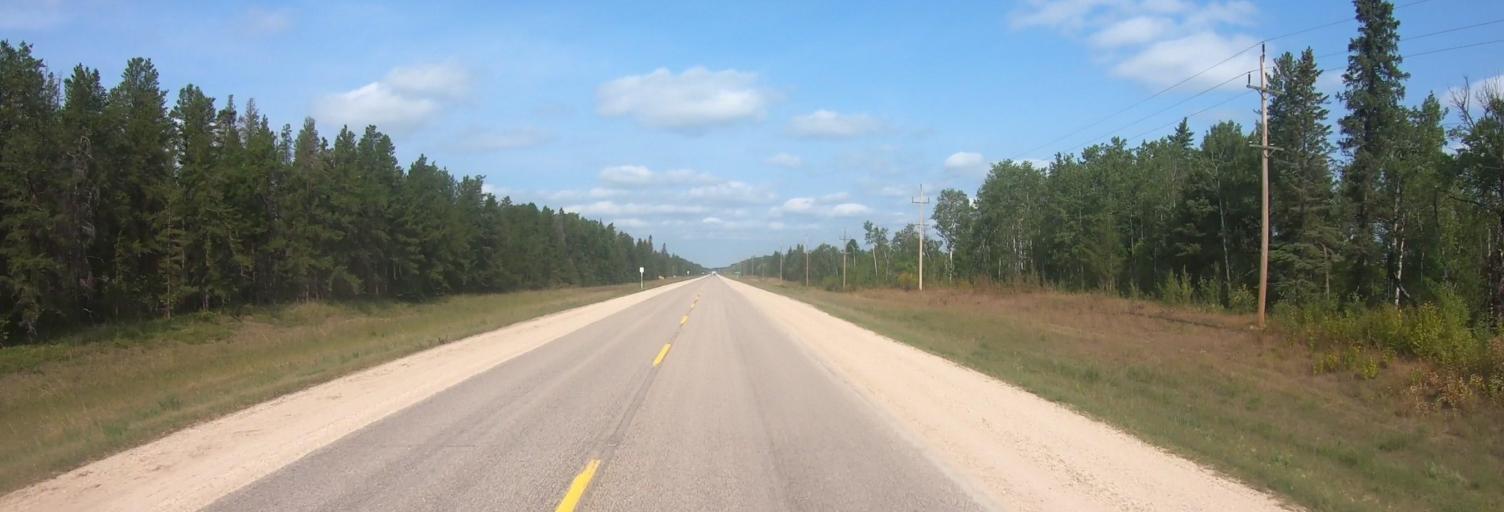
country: CA
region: Manitoba
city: La Broquerie
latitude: 49.1904
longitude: -96.2554
